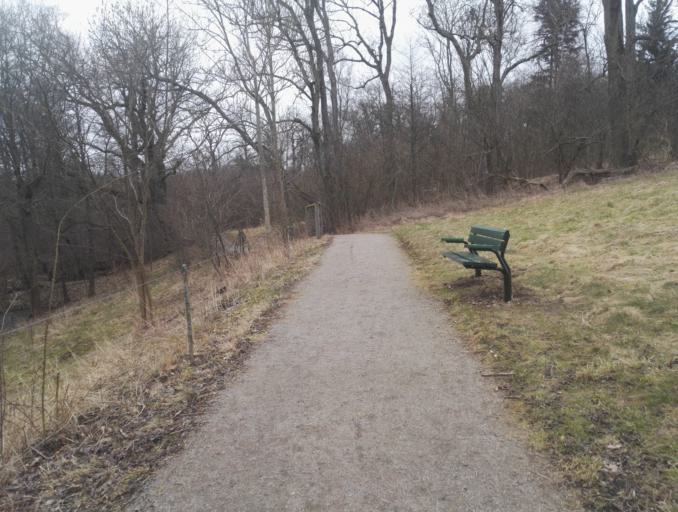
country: SE
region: Skane
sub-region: Helsingborg
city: Gantofta
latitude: 55.9989
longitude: 12.7893
